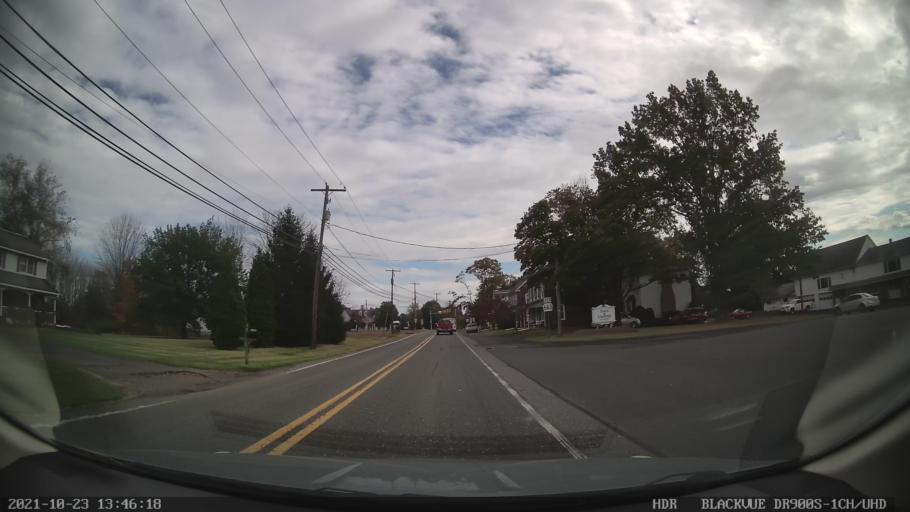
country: US
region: Pennsylvania
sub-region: Montgomery County
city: Pennsburg
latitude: 40.3761
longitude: -75.5172
